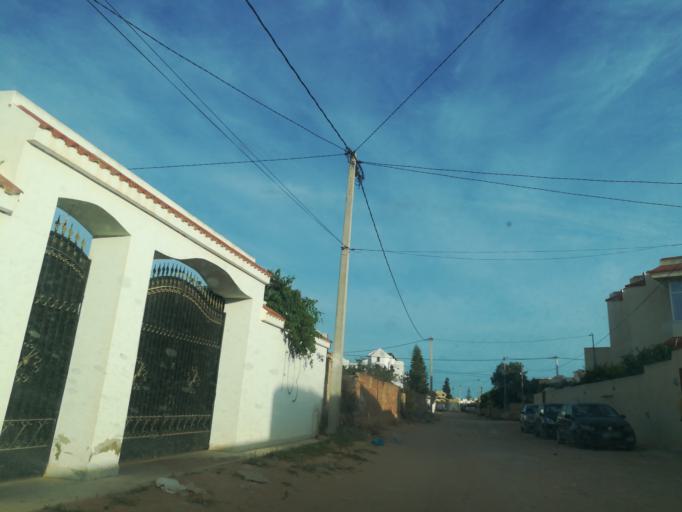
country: TN
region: Safaqis
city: Al Qarmadah
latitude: 34.8126
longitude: 10.7537
